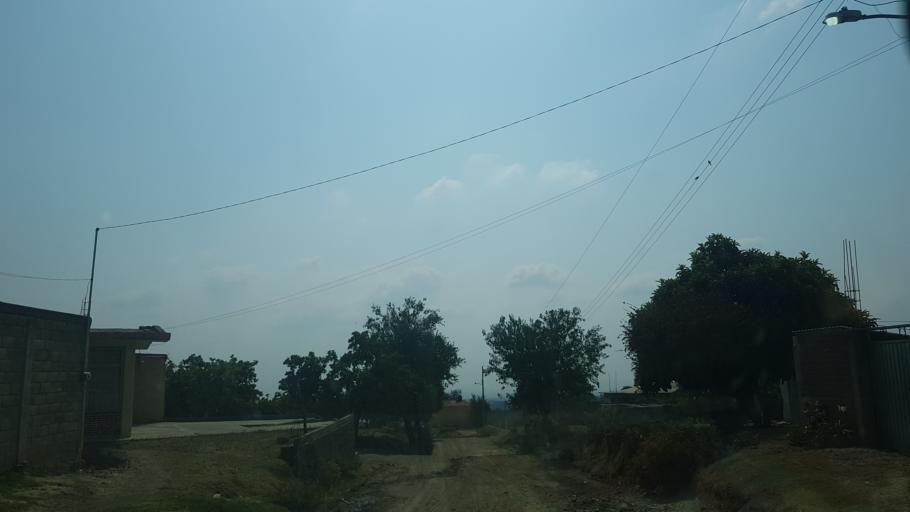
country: MX
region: Puebla
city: Domingo Arenas
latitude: 19.1296
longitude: -98.5027
